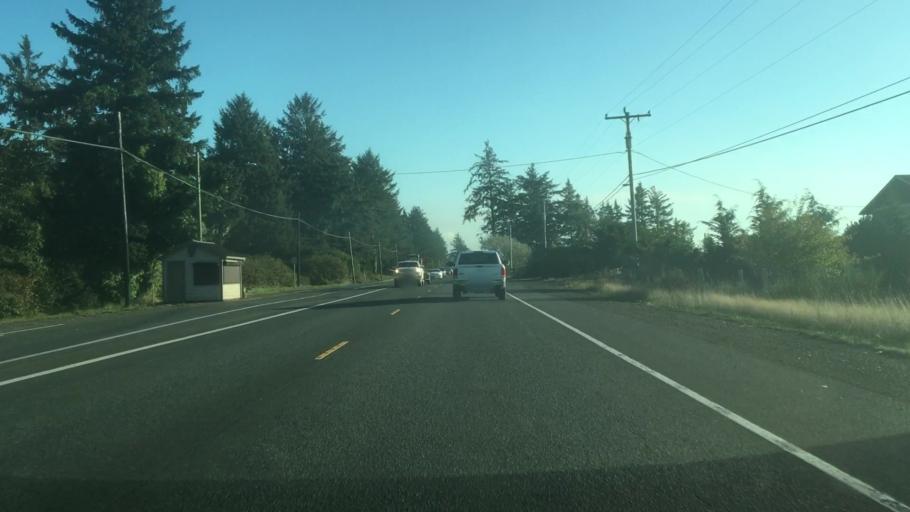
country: US
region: Oregon
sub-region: Clatsop County
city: Gearhart
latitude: 46.0890
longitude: -123.9165
